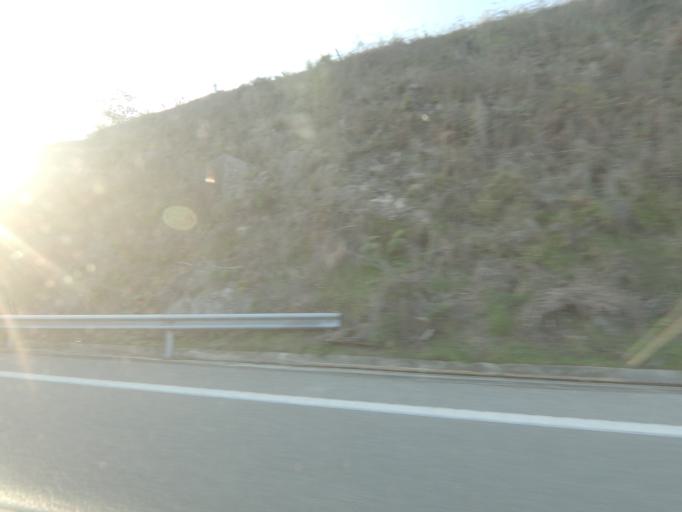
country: PT
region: Porto
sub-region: Amarante
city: Amarante
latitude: 41.2466
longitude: -8.1106
